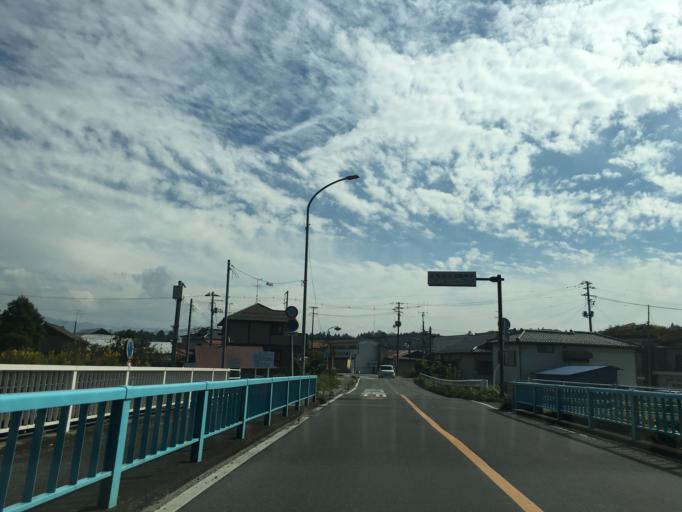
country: JP
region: Fukushima
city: Sukagawa
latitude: 37.2721
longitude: 140.4063
